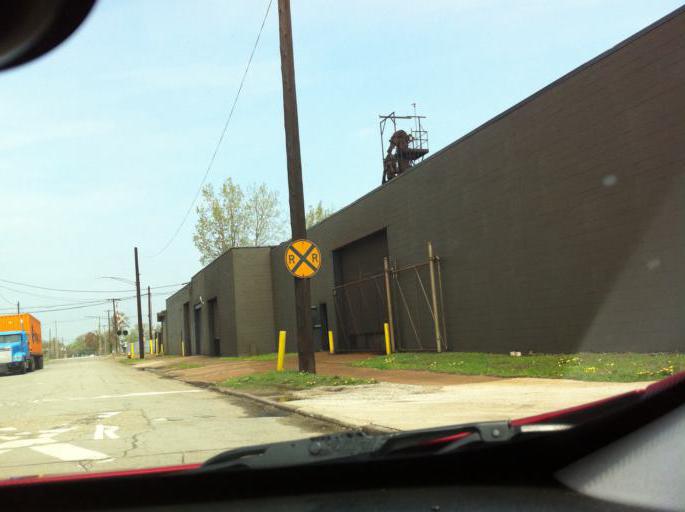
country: US
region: Michigan
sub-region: Wayne County
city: River Rouge
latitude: 42.3045
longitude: -83.0987
